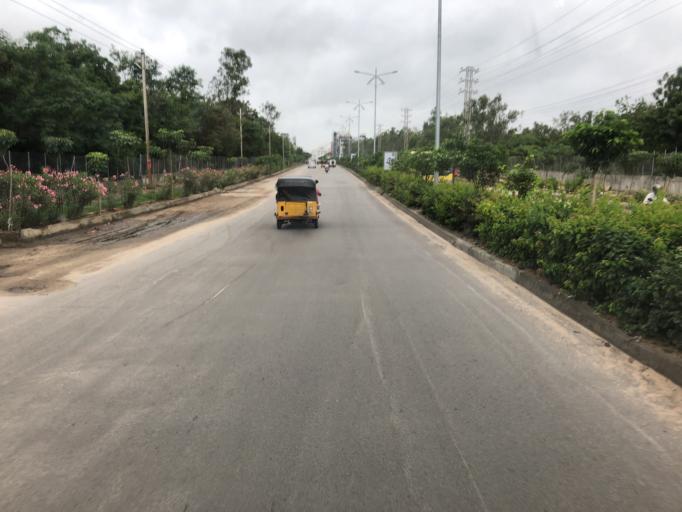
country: IN
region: Telangana
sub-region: Rangareddi
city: Kukatpalli
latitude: 17.4579
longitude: 78.3590
